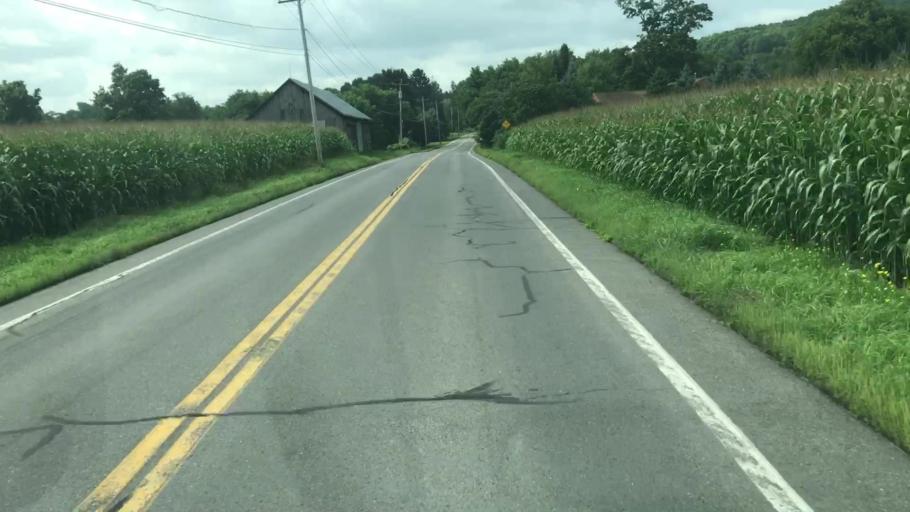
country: US
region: New York
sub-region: Onondaga County
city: Peru
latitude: 43.0601
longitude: -76.3641
